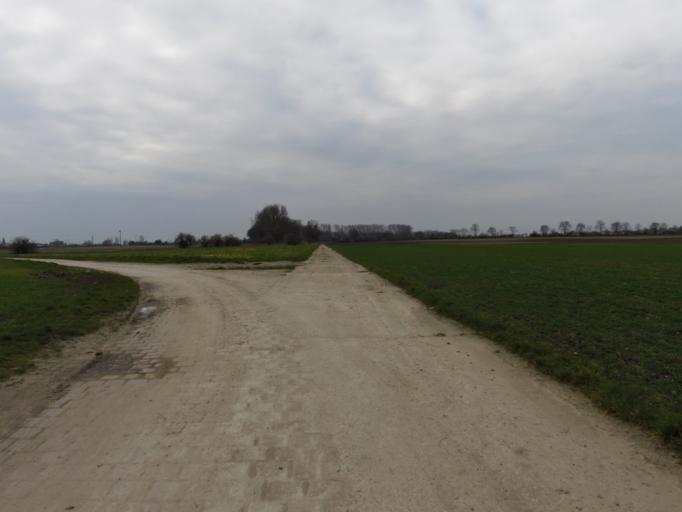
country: DE
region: Rheinland-Pfalz
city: Bobenheim-Roxheim
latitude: 49.5980
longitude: 8.3451
